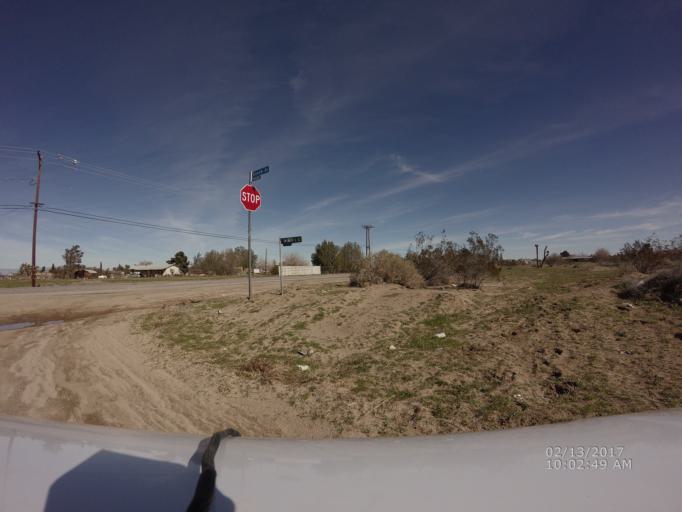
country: US
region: California
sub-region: Los Angeles County
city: Littlerock
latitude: 34.5543
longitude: -117.9716
